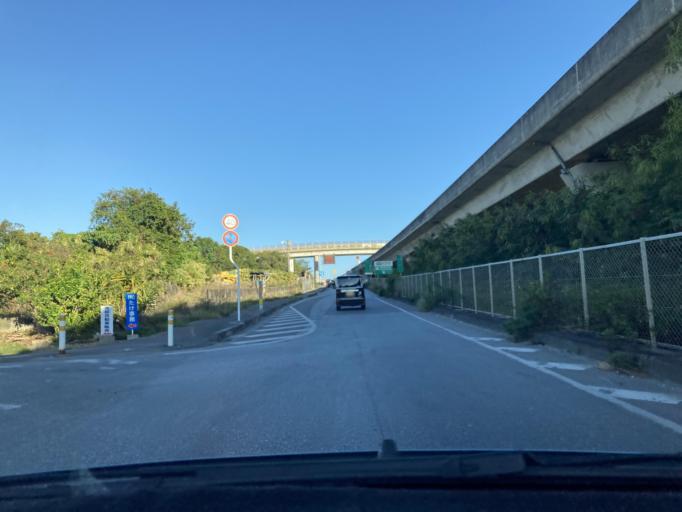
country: JP
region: Okinawa
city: Tomigusuku
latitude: 26.1811
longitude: 127.7249
